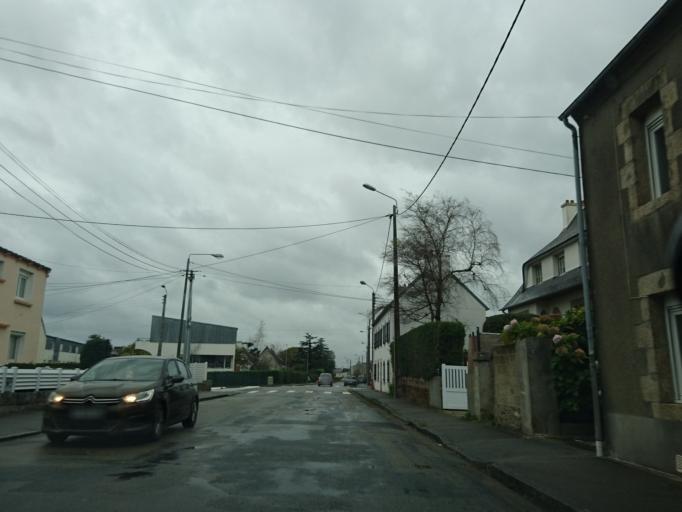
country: FR
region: Brittany
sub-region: Departement du Finistere
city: Brest
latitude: 48.4158
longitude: -4.4792
